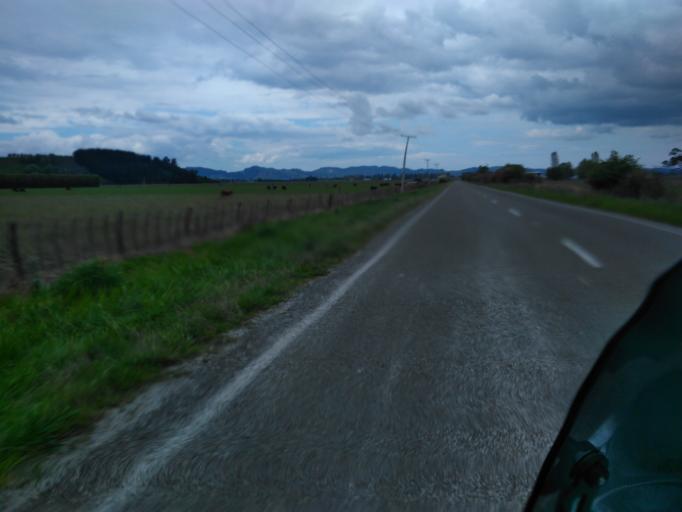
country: NZ
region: Gisborne
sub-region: Gisborne District
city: Gisborne
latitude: -38.6432
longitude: 177.8782
